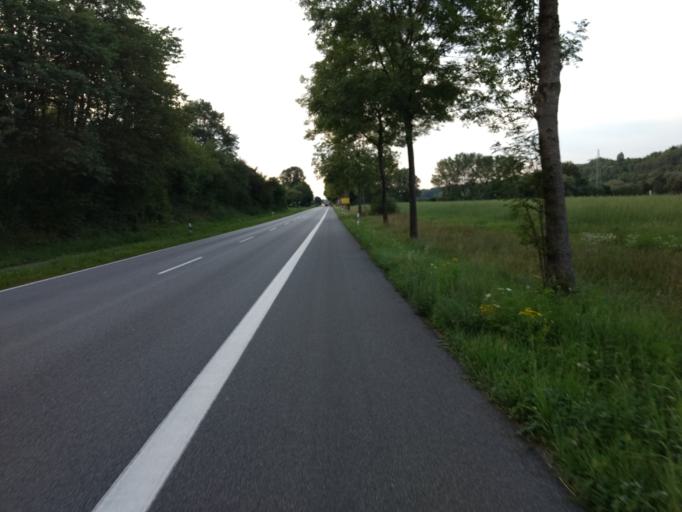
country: DE
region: Saarland
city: Rehlingen-Siersburg
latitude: 49.3954
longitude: 6.6614
